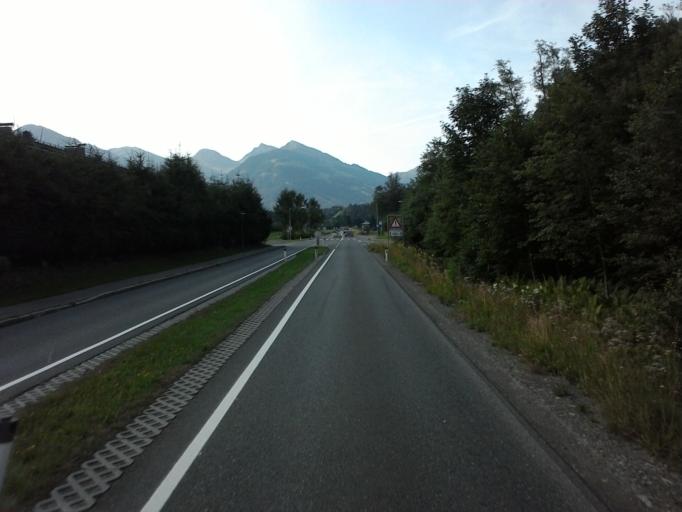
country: AT
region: Tyrol
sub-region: Politischer Bezirk Kitzbuhel
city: Kitzbuhel
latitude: 47.4299
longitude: 12.4093
